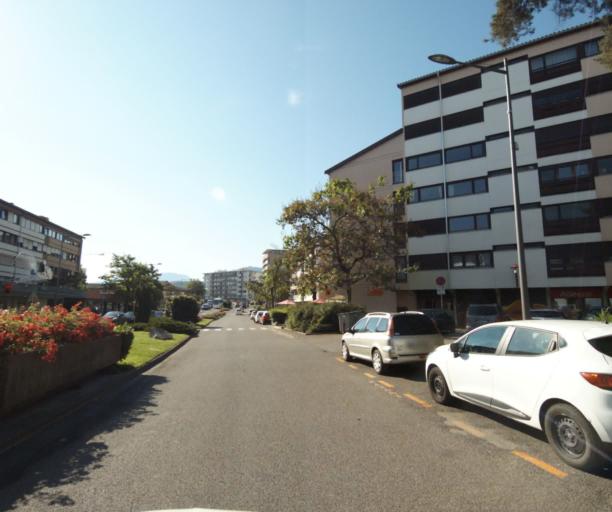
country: FR
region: Rhone-Alpes
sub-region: Departement de la Haute-Savoie
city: Thonon-les-Bains
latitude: 46.3736
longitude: 6.4813
